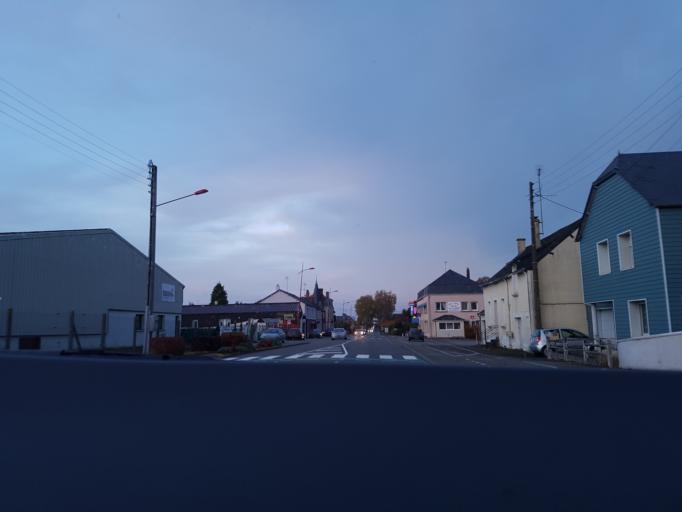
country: FR
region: Pays de la Loire
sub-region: Departement de la Mayenne
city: Cosse-le-Vivien
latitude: 47.9512
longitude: -0.9060
